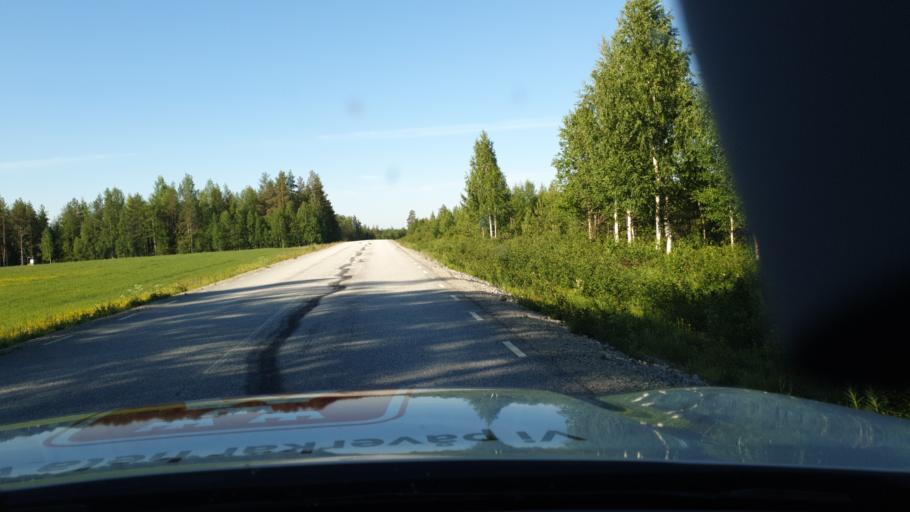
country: SE
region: Vaesterbotten
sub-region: Bjurholms Kommun
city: Bjurholm
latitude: 64.1517
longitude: 19.3506
